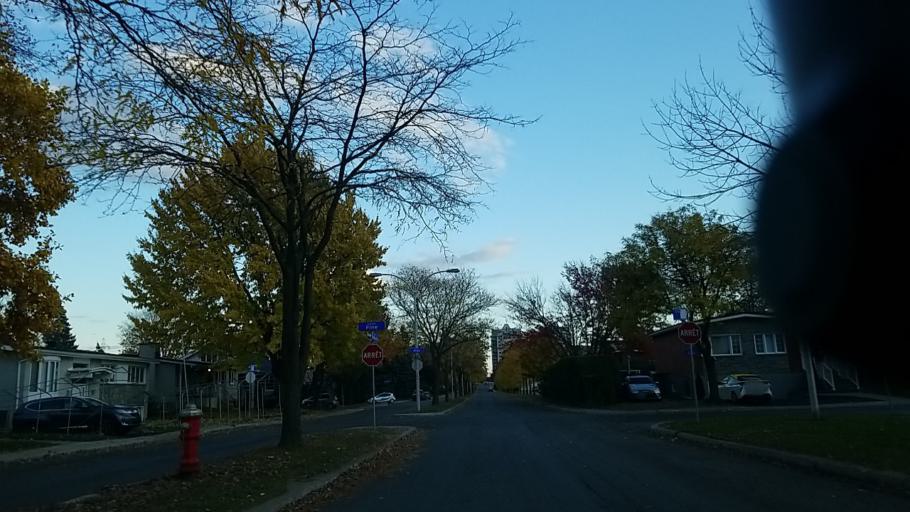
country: CA
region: Quebec
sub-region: Laval
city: Laval
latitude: 45.5740
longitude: -73.7269
